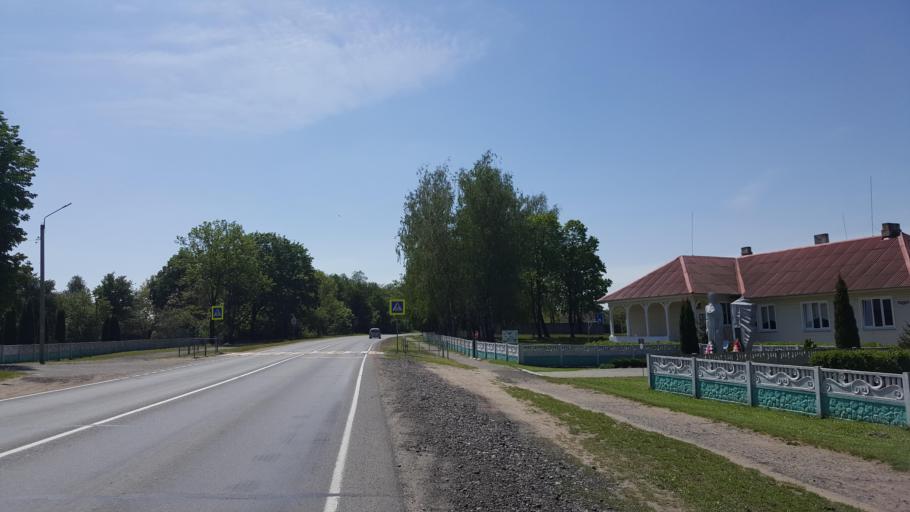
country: BY
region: Brest
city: Charnawchytsy
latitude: 52.2721
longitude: 23.7689
